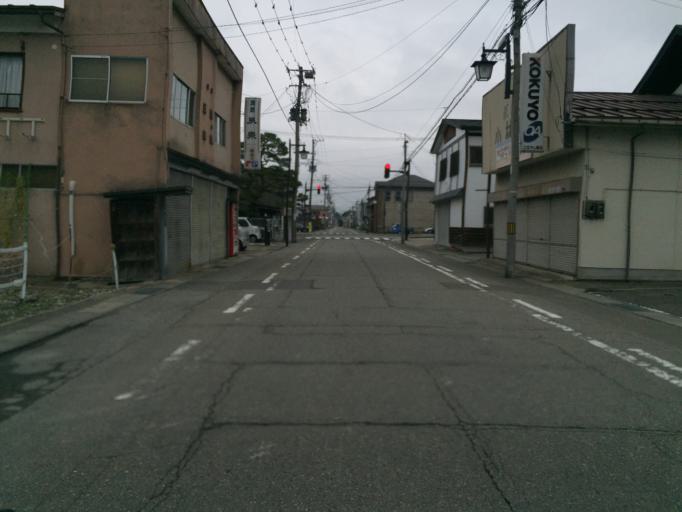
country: JP
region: Fukushima
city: Kitakata
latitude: 37.4990
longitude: 139.9349
